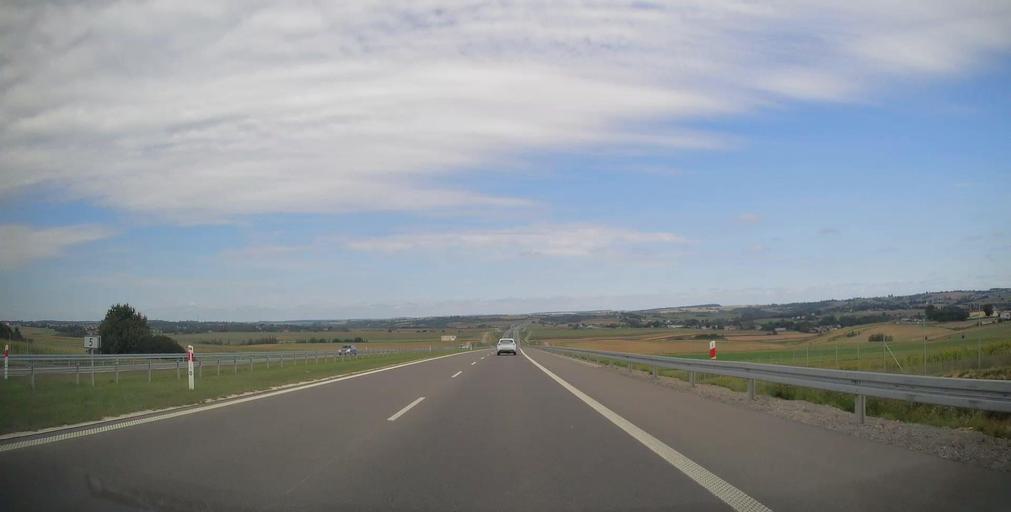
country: PL
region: Lesser Poland Voivodeship
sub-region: Powiat krakowski
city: Slomniki
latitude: 50.2758
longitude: 20.0211
